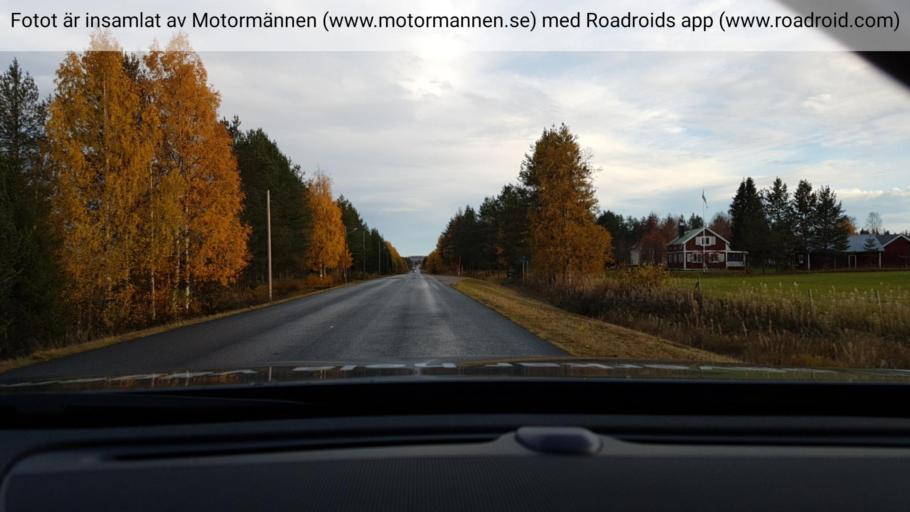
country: SE
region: Norrbotten
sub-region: Overkalix Kommun
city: OEverkalix
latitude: 66.9508
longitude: 22.7091
